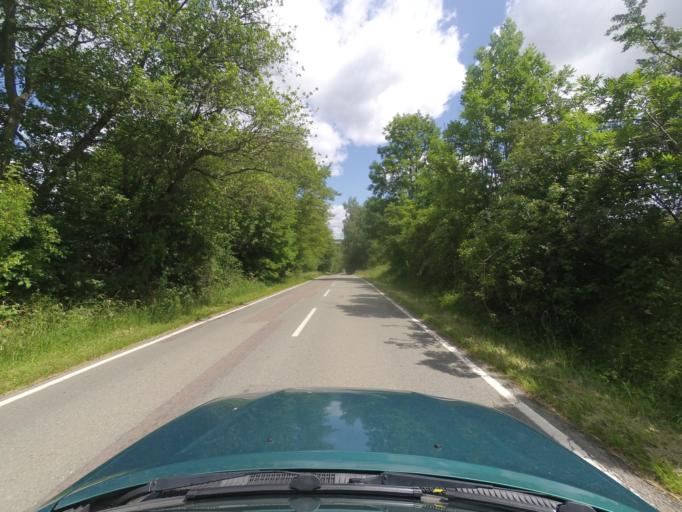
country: CZ
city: Dobruska
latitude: 50.3212
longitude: 16.2038
